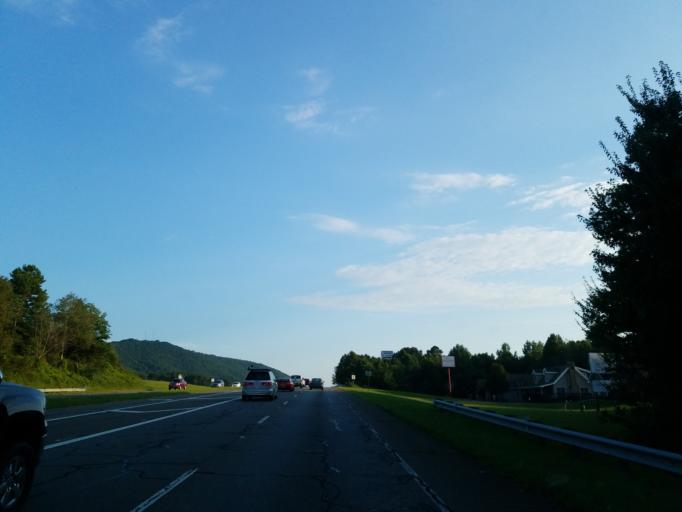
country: US
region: Georgia
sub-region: Gilmer County
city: Ellijay
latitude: 34.6488
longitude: -84.4963
